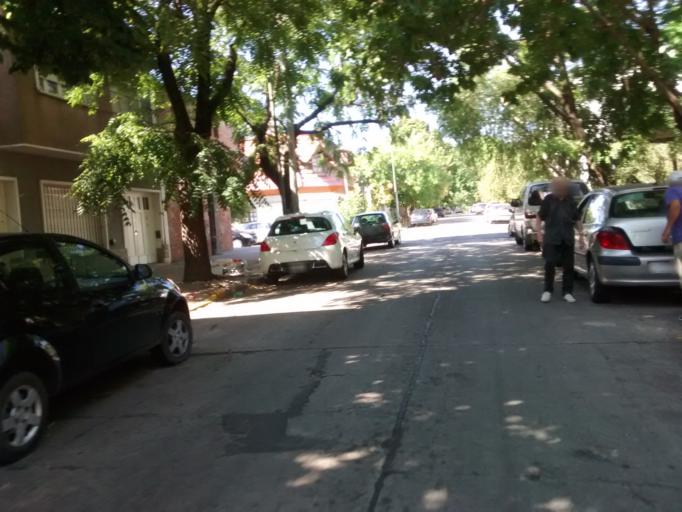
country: AR
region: Buenos Aires
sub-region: Partido de La Plata
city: La Plata
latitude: -34.9009
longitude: -57.9652
